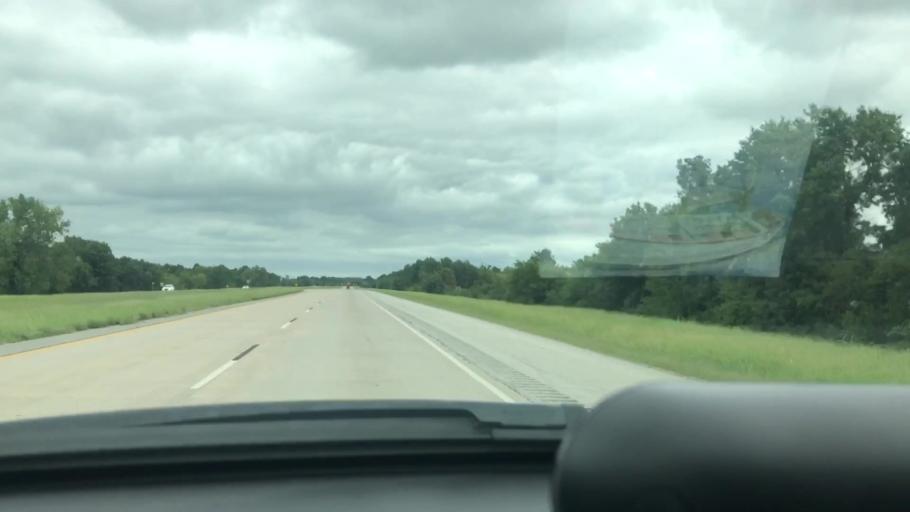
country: US
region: Oklahoma
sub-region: Wagoner County
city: Wagoner
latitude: 35.8986
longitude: -95.4026
